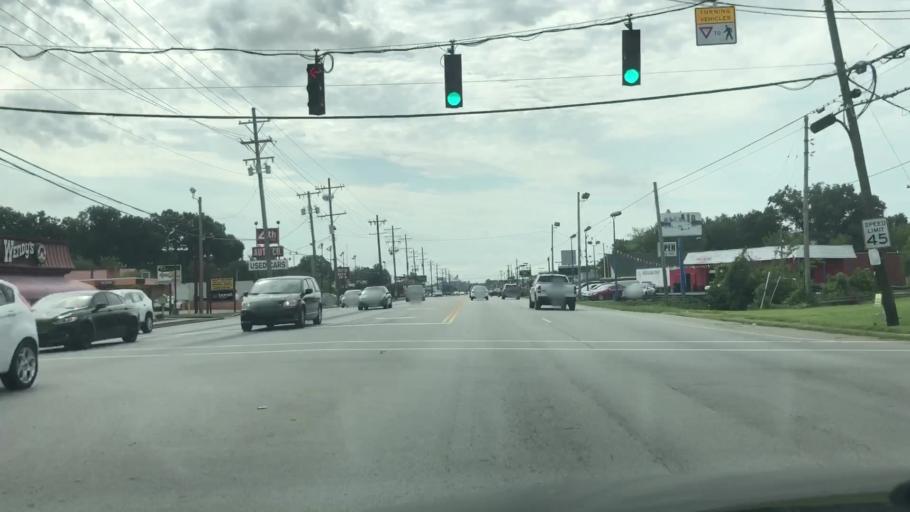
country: US
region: Kentucky
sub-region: Jefferson County
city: Audubon Park
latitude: 38.1747
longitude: -85.7128
